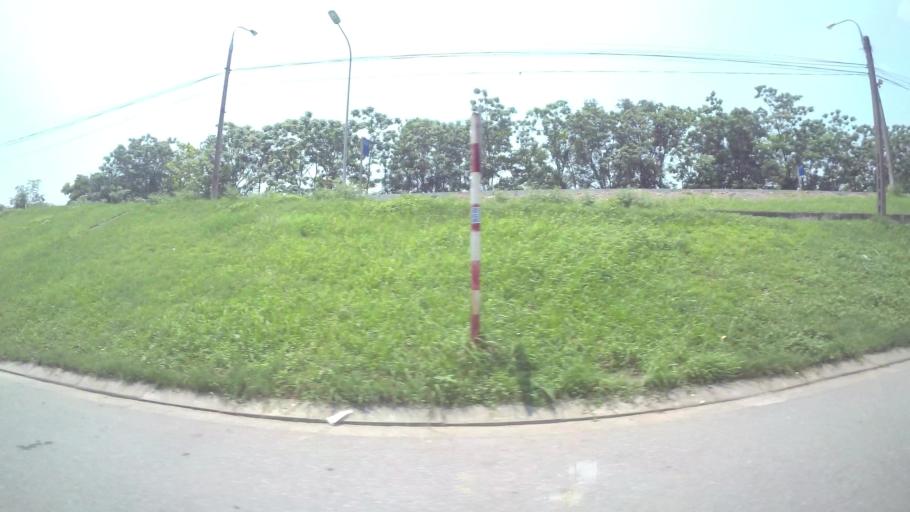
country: VN
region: Ha Noi
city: Hoan Kiem
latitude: 21.0241
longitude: 105.8859
